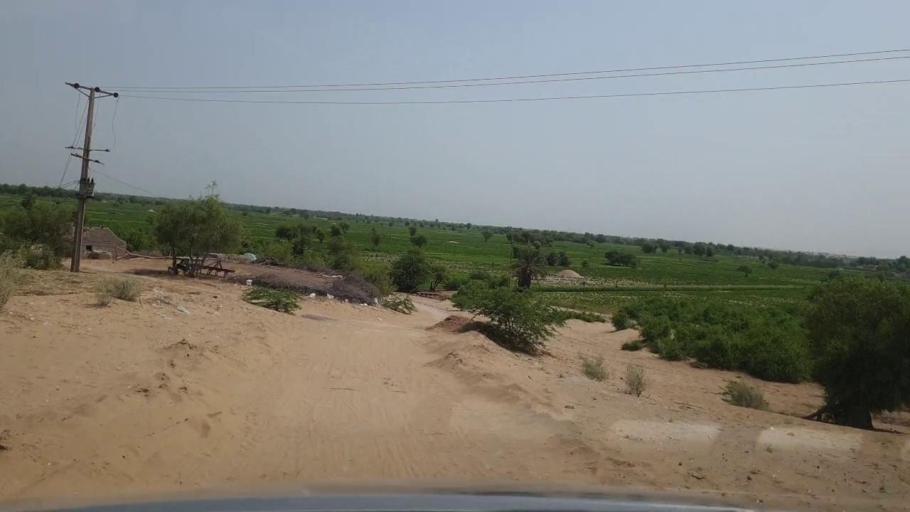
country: PK
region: Sindh
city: Pano Aqil
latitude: 27.6101
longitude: 69.1552
